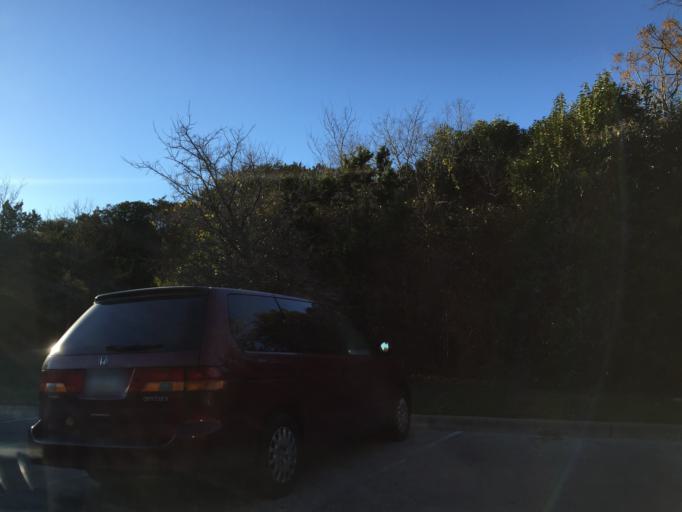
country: US
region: Texas
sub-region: Williamson County
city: Jollyville
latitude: 30.4317
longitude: -97.7817
